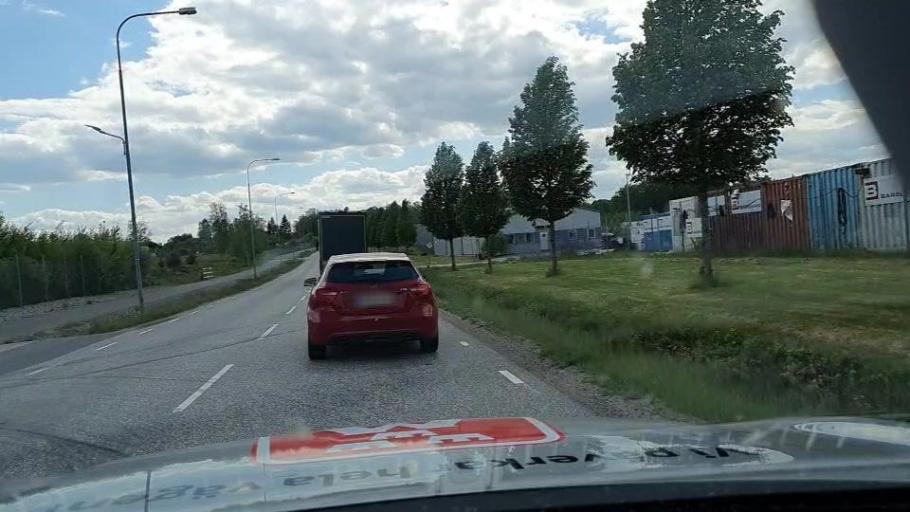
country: SE
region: Kronoberg
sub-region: Ljungby Kommun
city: Ljungby
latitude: 56.8459
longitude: 13.9210
